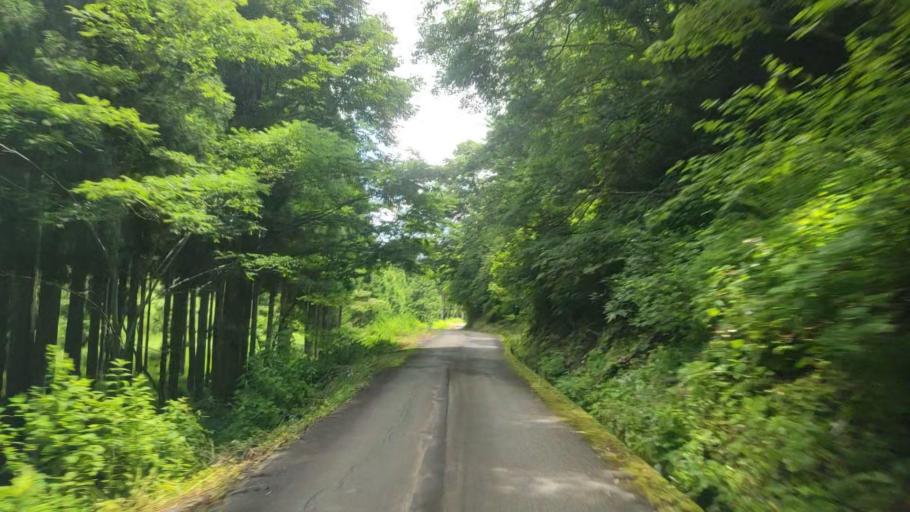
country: JP
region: Fukui
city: Ono
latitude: 35.8123
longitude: 136.4615
